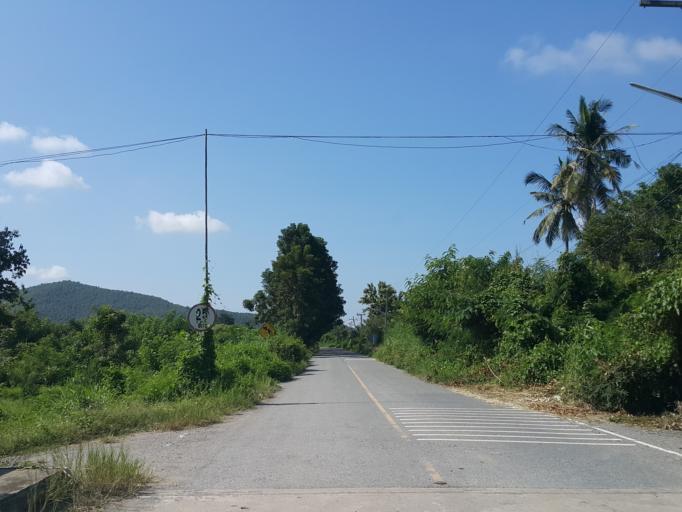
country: TH
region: Chiang Mai
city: Mae On
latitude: 18.7897
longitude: 99.1842
